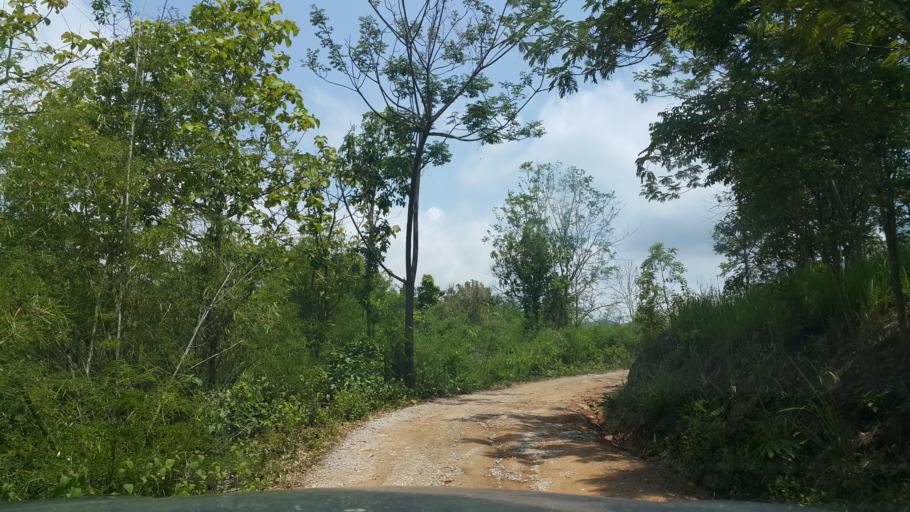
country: TH
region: Chiang Rai
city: Chiang Rai
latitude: 19.9991
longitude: 99.7175
